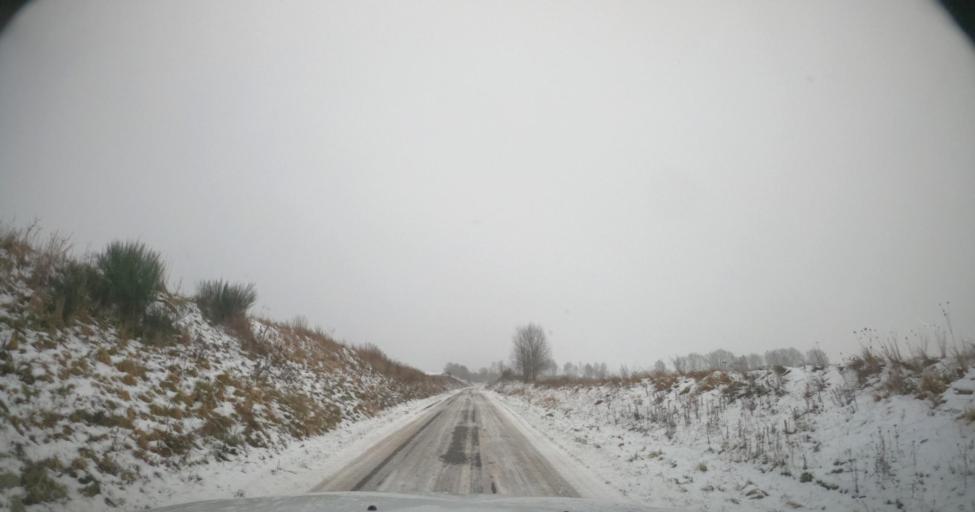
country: PL
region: West Pomeranian Voivodeship
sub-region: Powiat gryficki
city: Brojce
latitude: 53.9066
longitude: 15.3553
